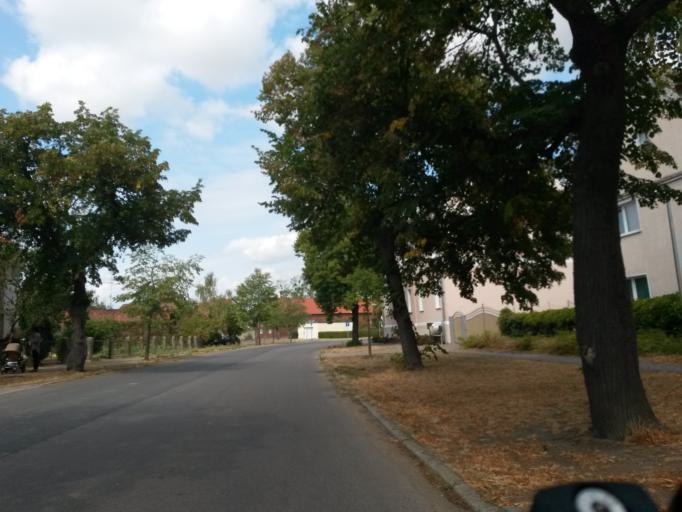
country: DE
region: Saxony-Anhalt
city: Muhlanger
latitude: 51.8343
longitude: 12.7069
